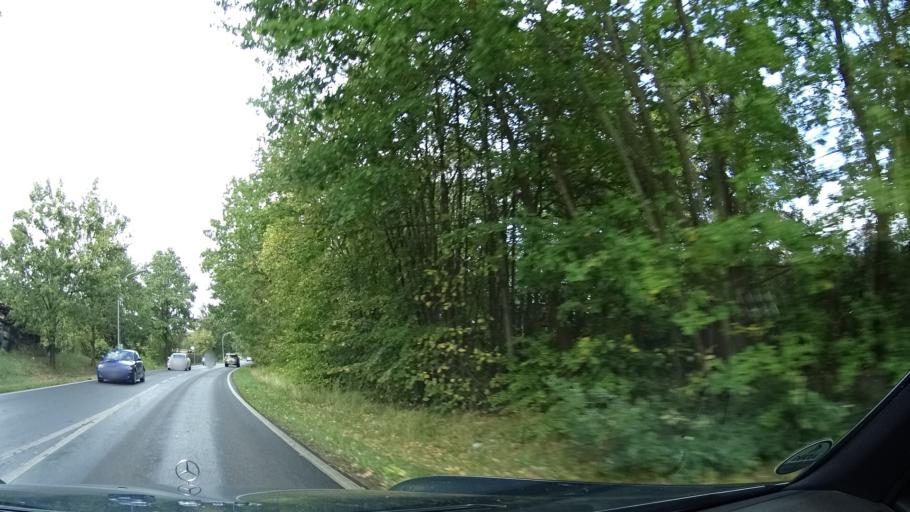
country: DE
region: Brandenburg
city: Neuruppin
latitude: 52.9002
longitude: 12.7999
